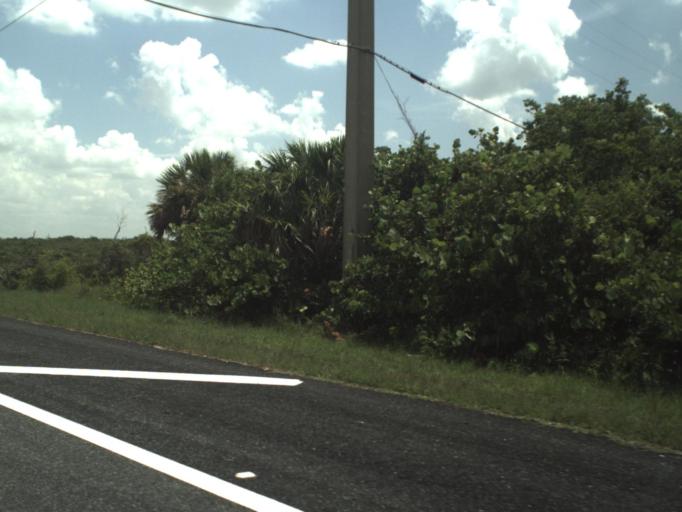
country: US
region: Florida
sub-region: Martin County
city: Hobe Sound
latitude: 27.0243
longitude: -80.1089
